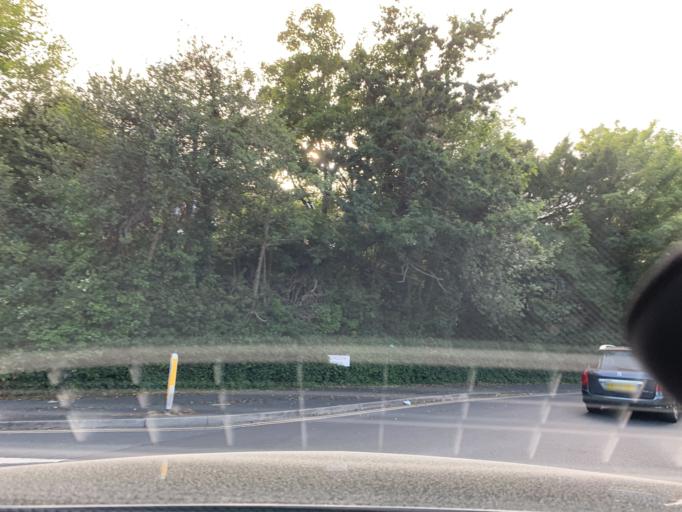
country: GB
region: England
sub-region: East Sussex
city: Saint Leonards-on-Sea
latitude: 50.8646
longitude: 0.5571
